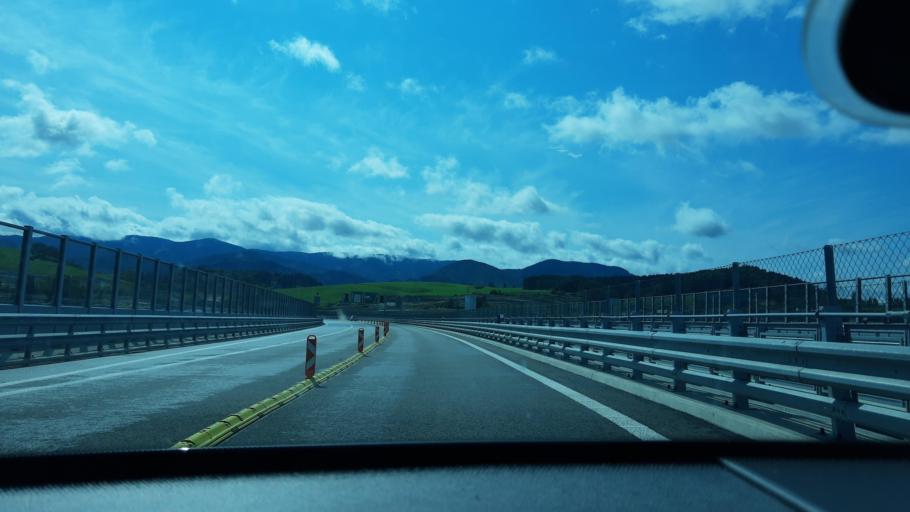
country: SK
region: Zilinsky
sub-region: Okres Zilina
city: Zilina
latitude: 49.1802
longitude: 18.7238
